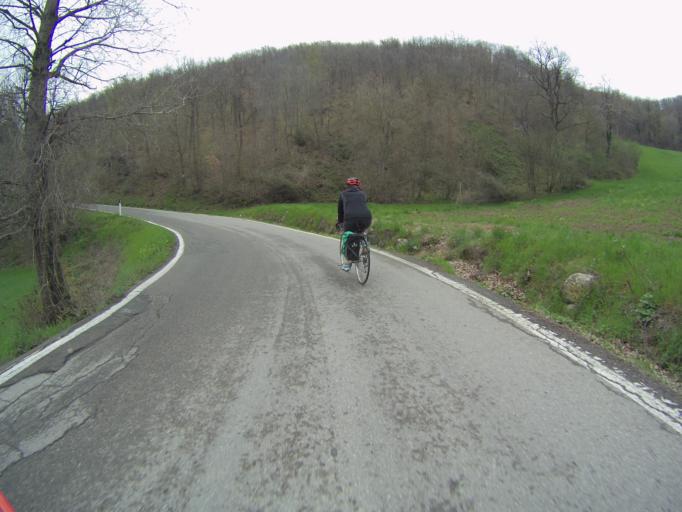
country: IT
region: Emilia-Romagna
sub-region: Provincia di Reggio Emilia
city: Ciano d'Enza
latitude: 44.5630
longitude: 10.4506
